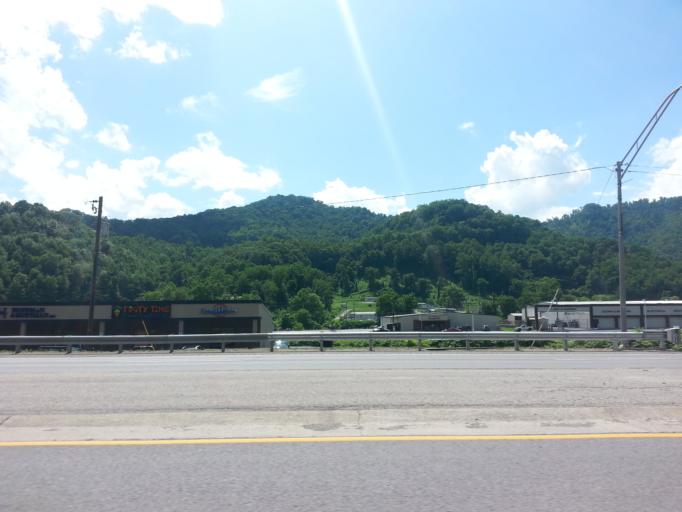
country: US
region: Kentucky
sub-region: Harlan County
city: Harlan
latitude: 36.8336
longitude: -83.3249
